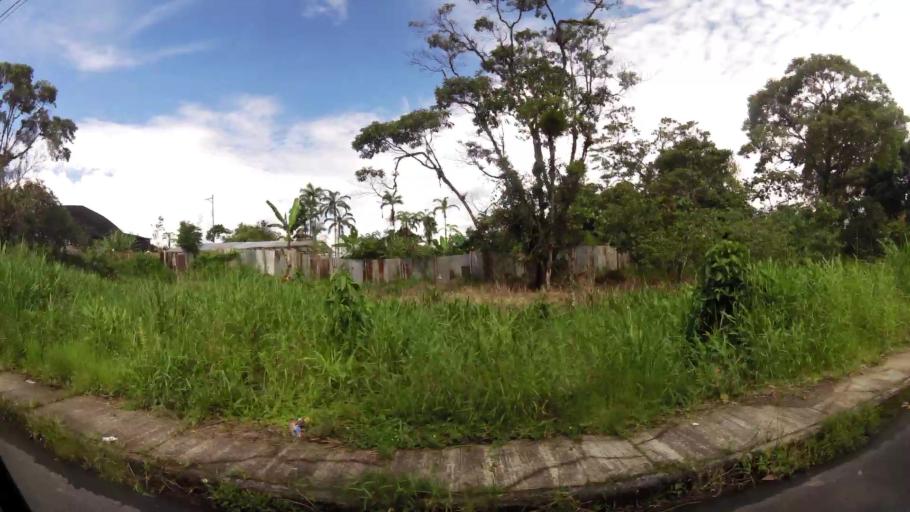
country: EC
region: Pastaza
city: Puyo
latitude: -1.5011
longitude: -78.0644
